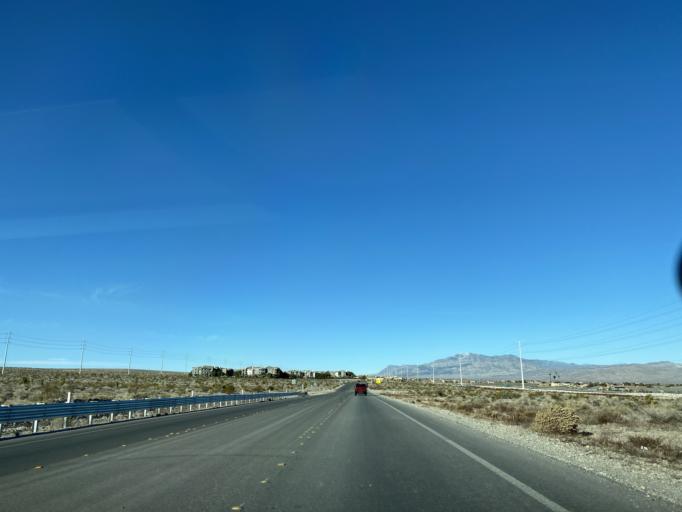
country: US
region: Nevada
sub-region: Clark County
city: Summerlin South
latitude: 36.2682
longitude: -115.3300
